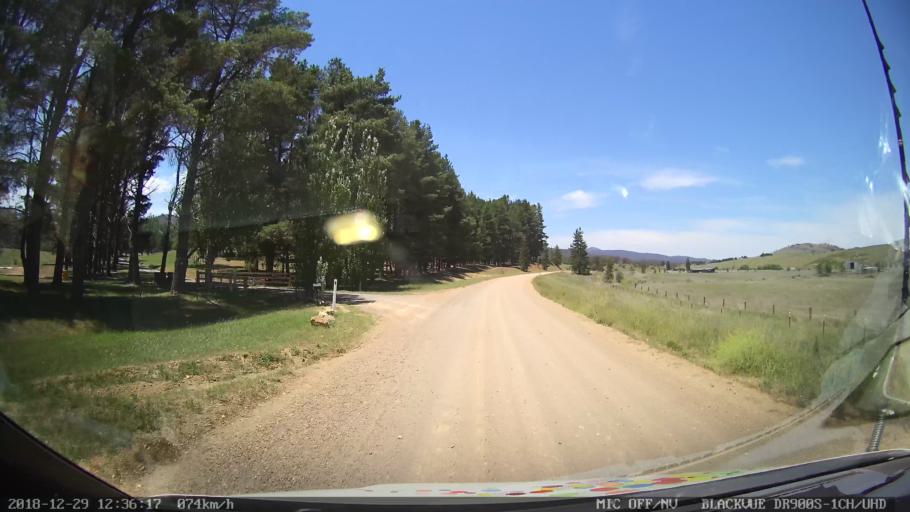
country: AU
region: Australian Capital Territory
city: Macarthur
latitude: -35.5691
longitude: 149.2262
